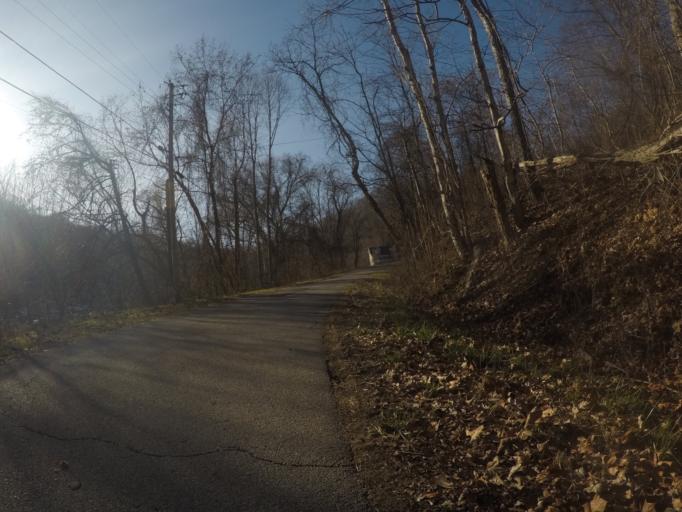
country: US
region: West Virginia
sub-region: Cabell County
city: Huntington
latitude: 38.3911
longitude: -82.4868
